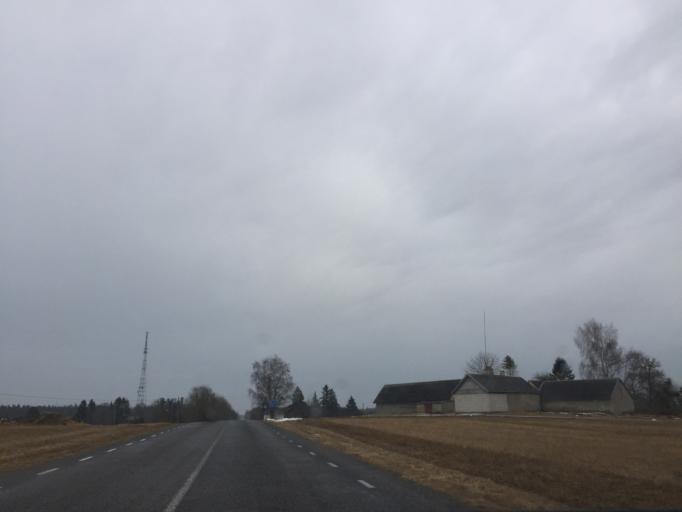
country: EE
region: Saare
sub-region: Orissaare vald
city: Orissaare
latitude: 58.5630
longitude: 23.0461
